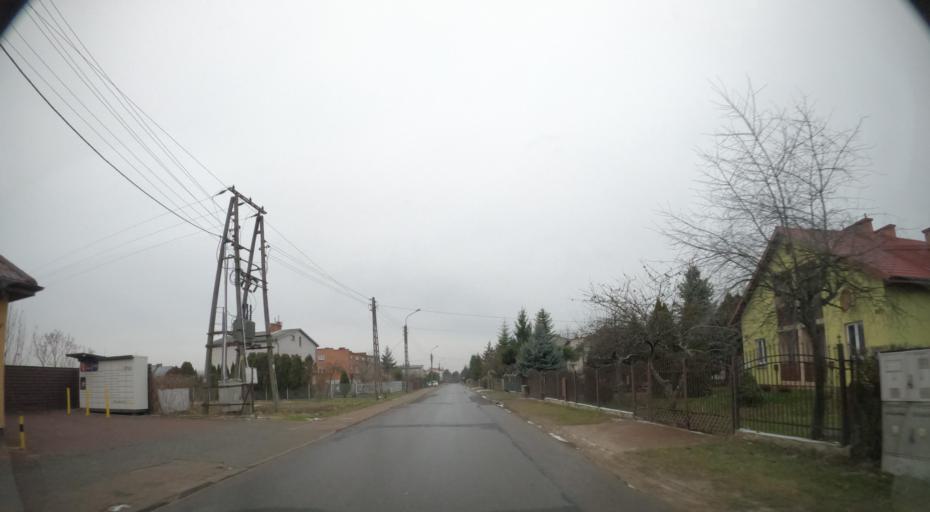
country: PL
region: Masovian Voivodeship
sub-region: Radom
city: Radom
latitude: 51.3819
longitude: 21.1958
